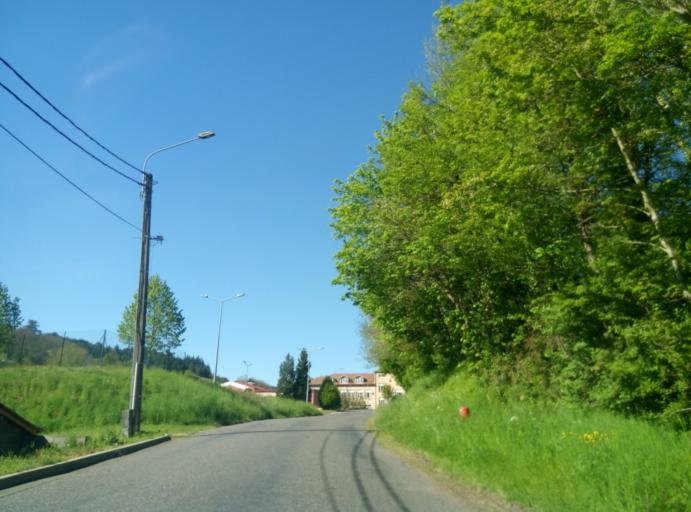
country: FR
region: Rhone-Alpes
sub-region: Departement du Rhone
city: Grandris
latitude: 46.0600
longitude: 4.4915
